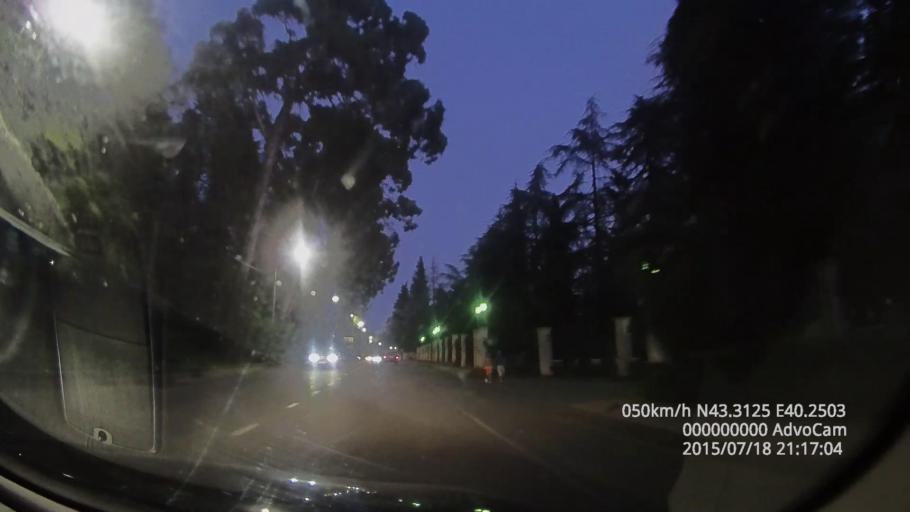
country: GE
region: Abkhazia
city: Gagra
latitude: 43.3123
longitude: 40.2505
